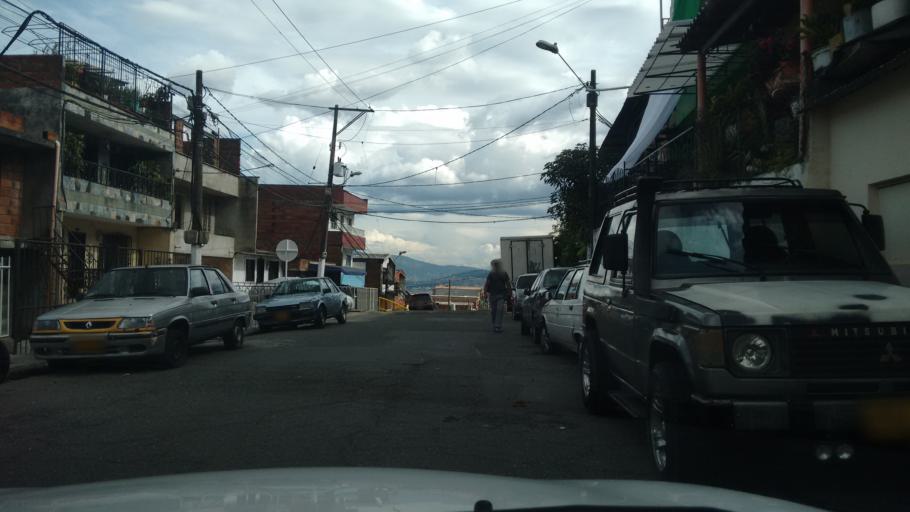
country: CO
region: Antioquia
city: Bello
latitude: 6.2958
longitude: -75.5795
